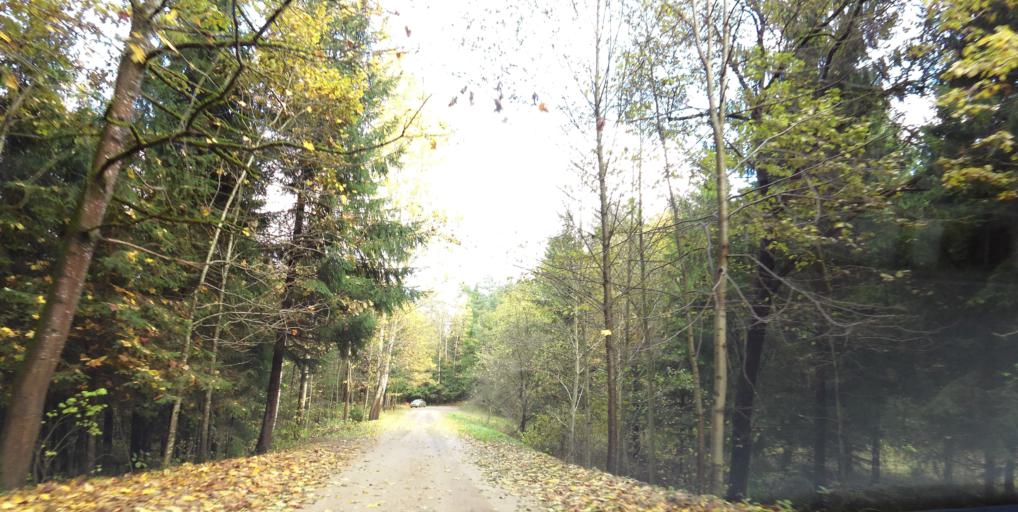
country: LT
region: Vilnius County
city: Vilkpede
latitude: 54.6515
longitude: 25.2527
